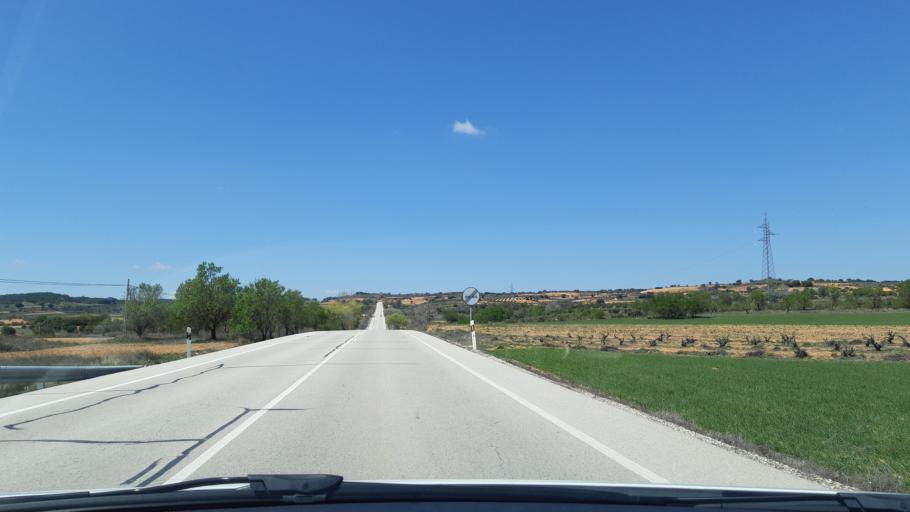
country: ES
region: Castille-La Mancha
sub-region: Provincia de Guadalajara
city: Cifuentes
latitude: 40.7892
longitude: -2.6364
